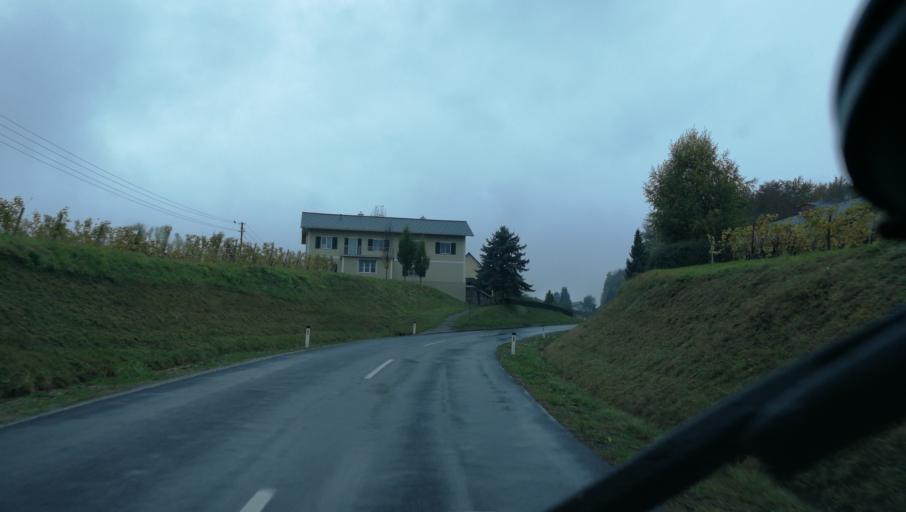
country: AT
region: Styria
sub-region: Politischer Bezirk Leibnitz
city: Spielfeld
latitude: 46.7022
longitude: 15.6225
